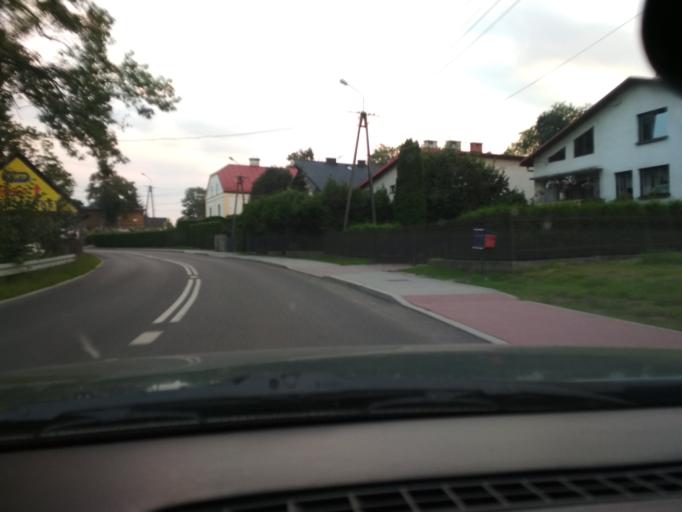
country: PL
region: Silesian Voivodeship
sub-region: Powiat bielski
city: Jasienica
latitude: 49.8445
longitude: 18.9418
